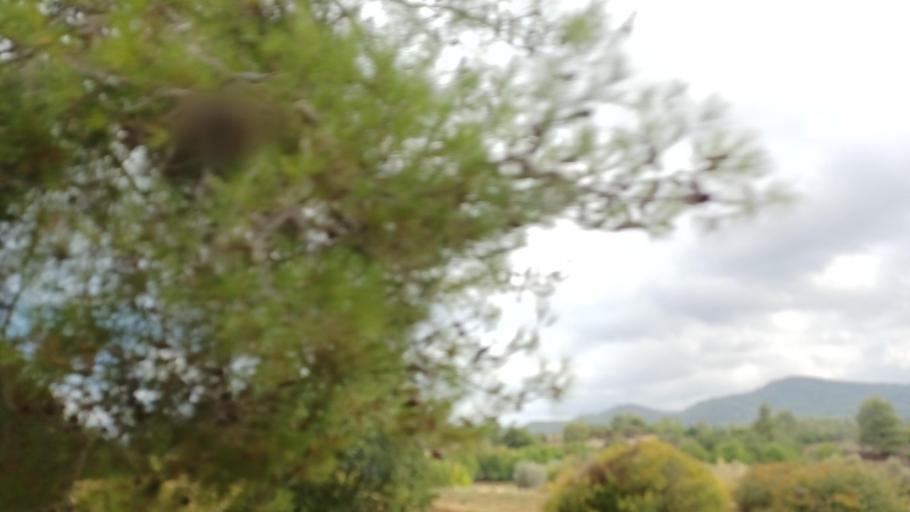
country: CY
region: Pafos
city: Polis
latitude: 35.0095
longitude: 32.4951
